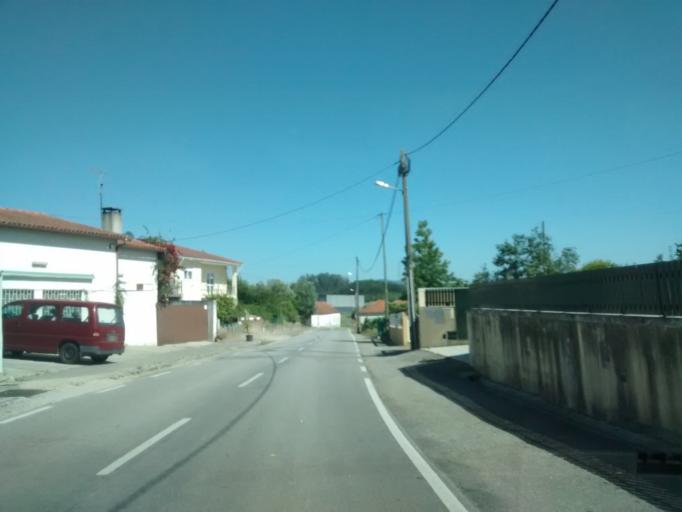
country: PT
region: Aveiro
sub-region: Anadia
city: Sangalhos
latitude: 40.4405
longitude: -8.5015
